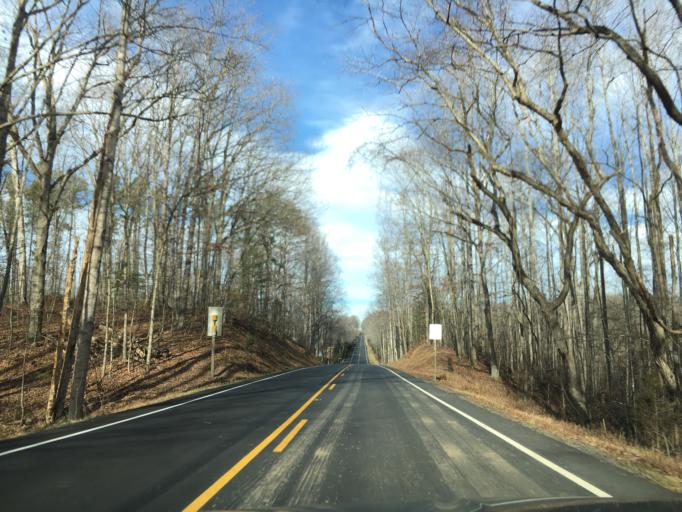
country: US
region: Virginia
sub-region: Orange County
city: Orange
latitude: 38.2481
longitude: -77.9531
